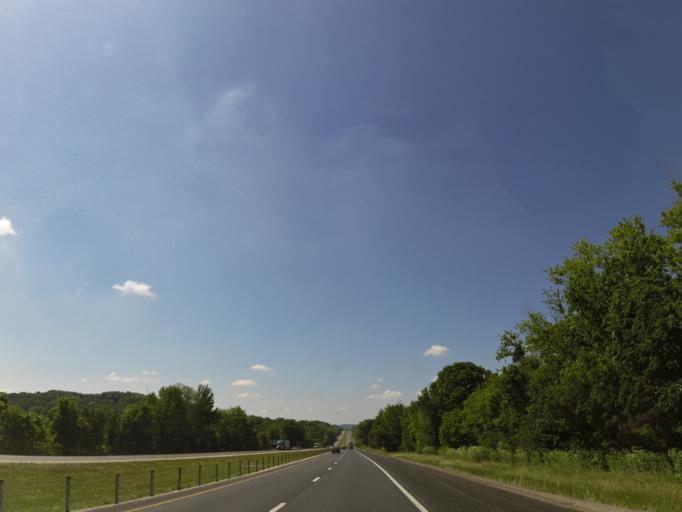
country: US
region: Kentucky
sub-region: Rockcastle County
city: Brodhead
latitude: 37.4270
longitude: -84.3436
